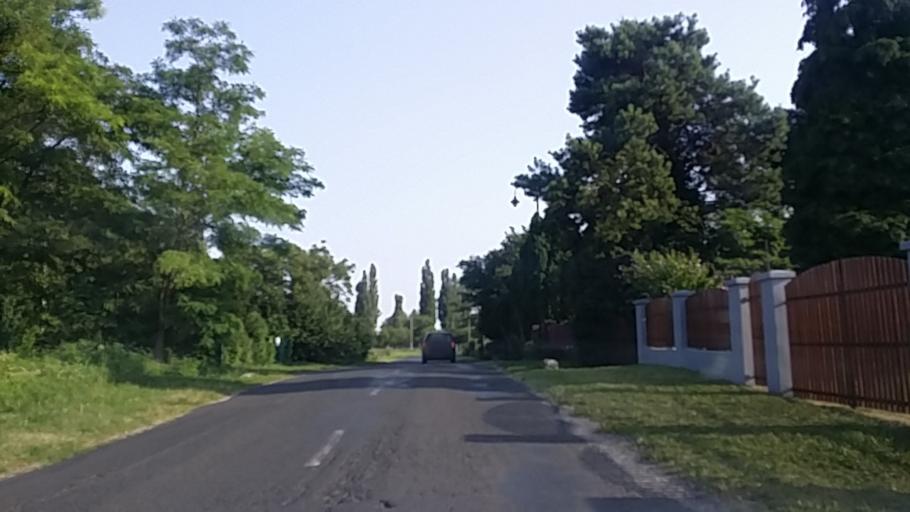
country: HU
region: Veszprem
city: Badacsonytomaj
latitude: 46.7937
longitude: 17.4495
